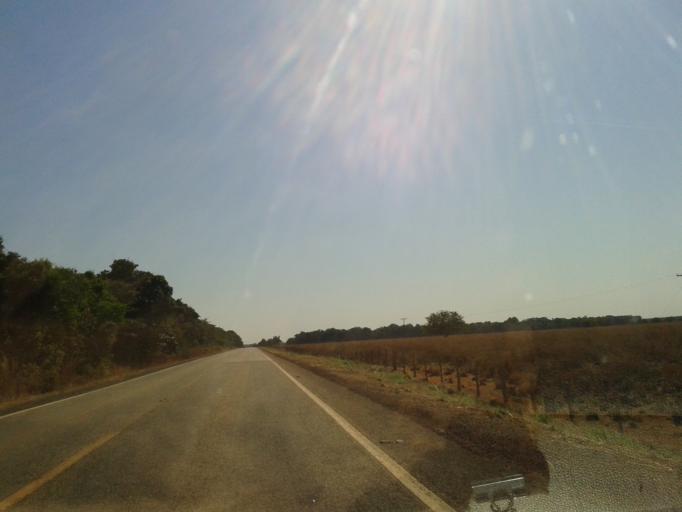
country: BR
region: Goias
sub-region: Mozarlandia
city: Mozarlandia
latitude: -14.3226
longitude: -50.4107
